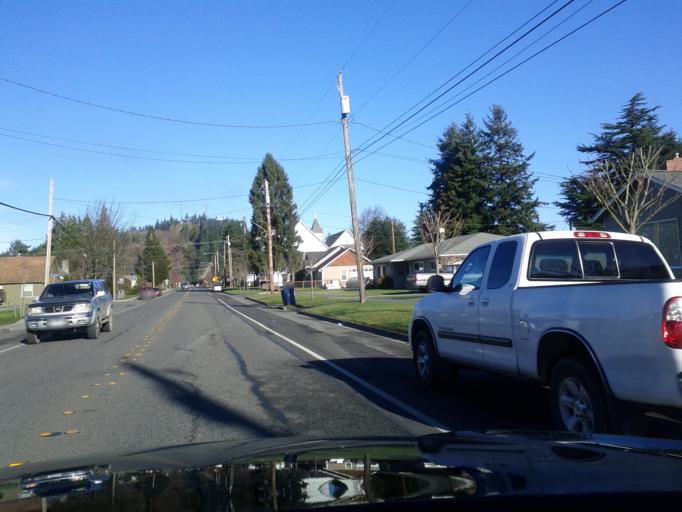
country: US
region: Washington
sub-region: Skagit County
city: Burlington
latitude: 48.4701
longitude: -122.3248
